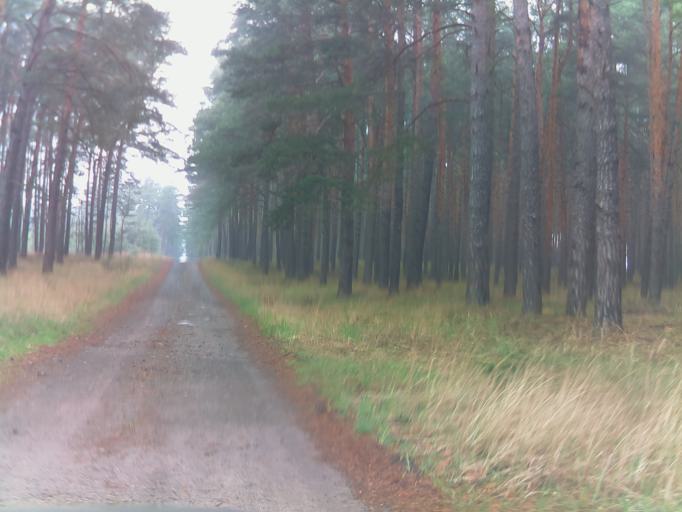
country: DE
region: Brandenburg
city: Lieberose
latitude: 52.0272
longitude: 14.2288
